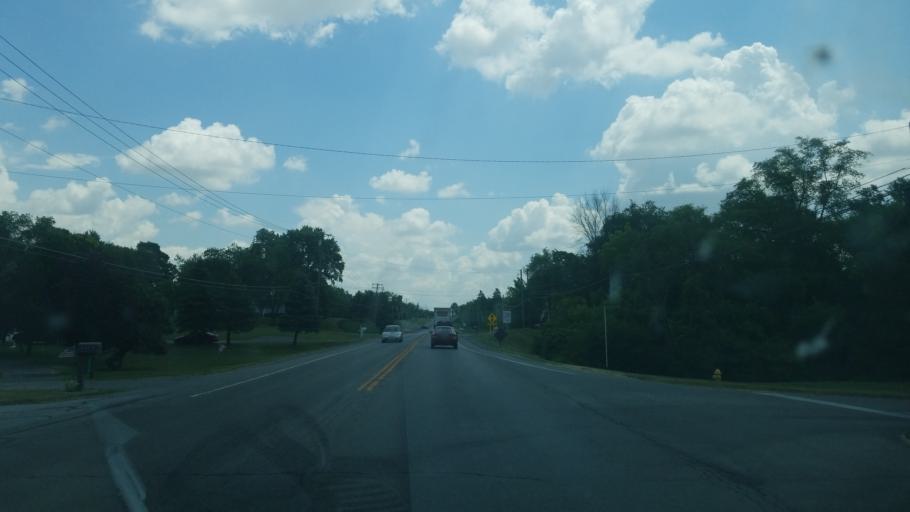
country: US
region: Ohio
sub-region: Allen County
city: Lima
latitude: 40.7311
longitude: -84.0359
